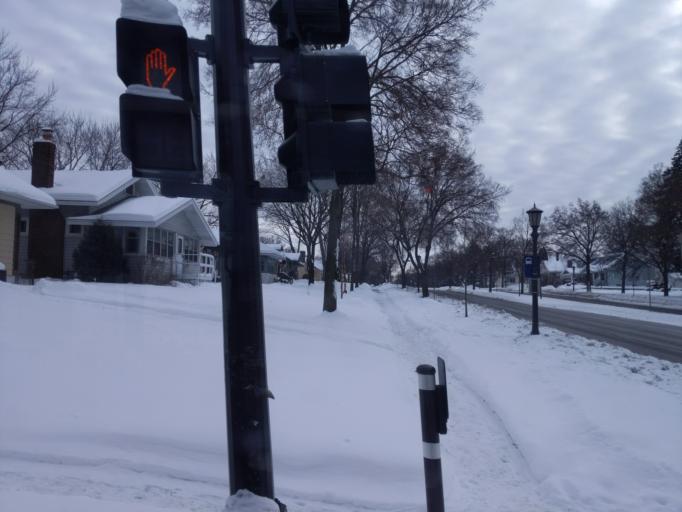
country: US
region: Minnesota
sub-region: Ramsey County
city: Falcon Heights
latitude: 44.9630
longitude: -93.1464
